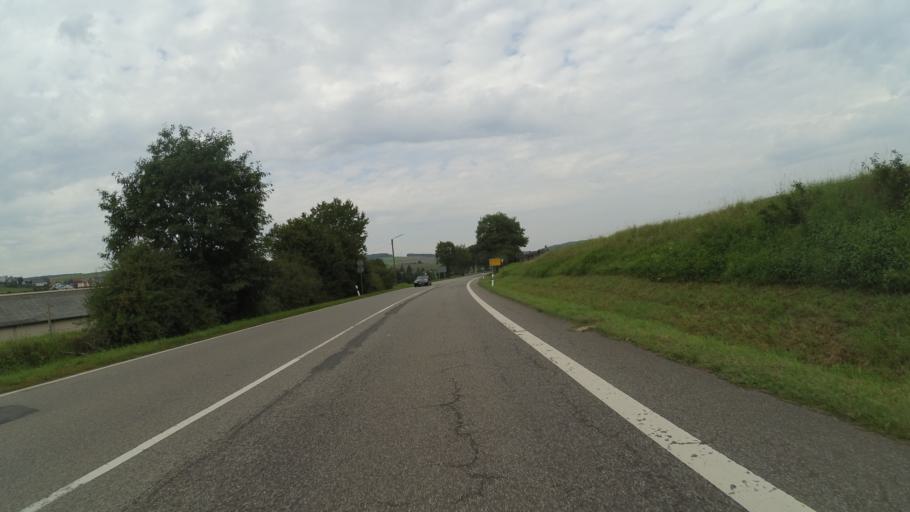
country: DE
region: Rheinland-Pfalz
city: Zerf
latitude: 49.5874
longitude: 6.6773
